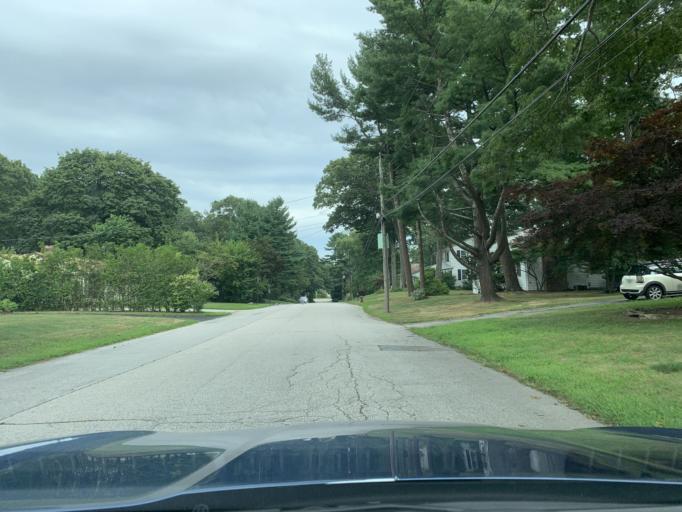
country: US
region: Rhode Island
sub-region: Kent County
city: East Greenwich
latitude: 41.6114
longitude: -71.4687
